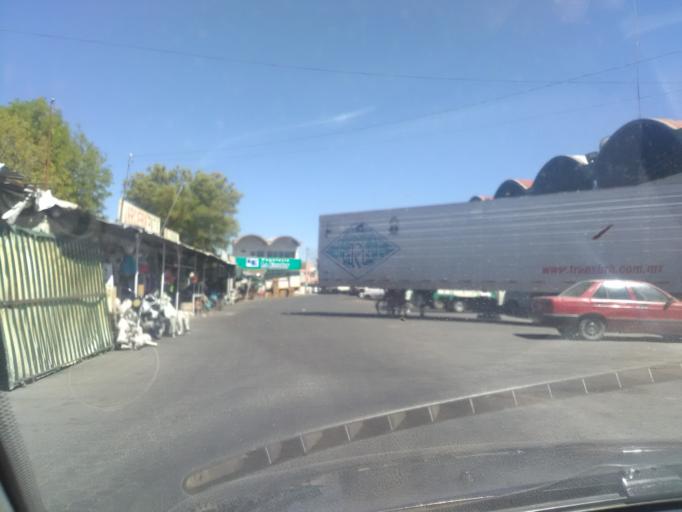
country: MX
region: Durango
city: Victoria de Durango
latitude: 24.0161
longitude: -104.6601
